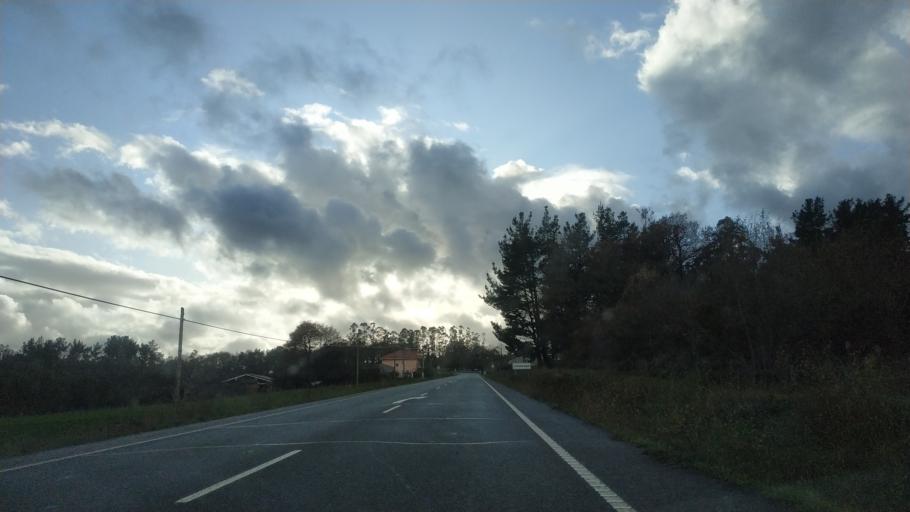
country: ES
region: Galicia
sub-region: Provincia da Coruna
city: Arzua
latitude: 42.8797
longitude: -8.2013
